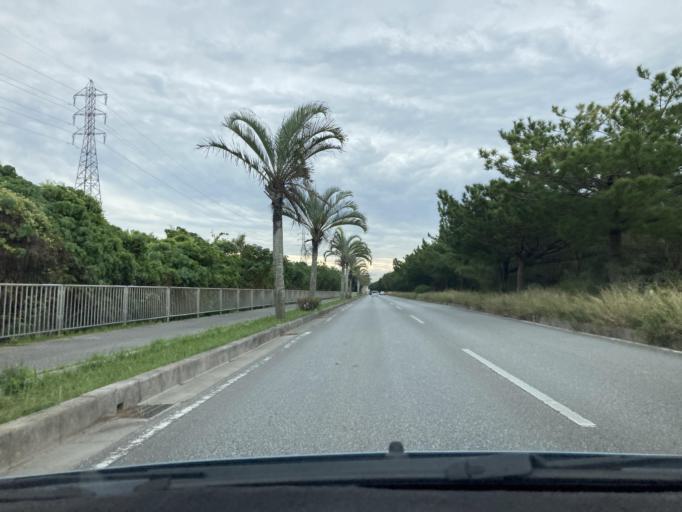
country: JP
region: Okinawa
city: Okinawa
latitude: 26.3906
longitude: 127.7552
